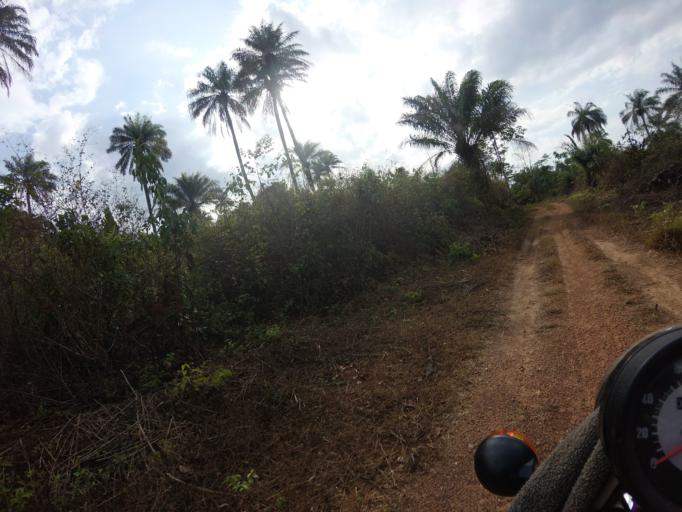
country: SL
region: Southern Province
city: Zimmi
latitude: 7.1498
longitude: -11.2050
